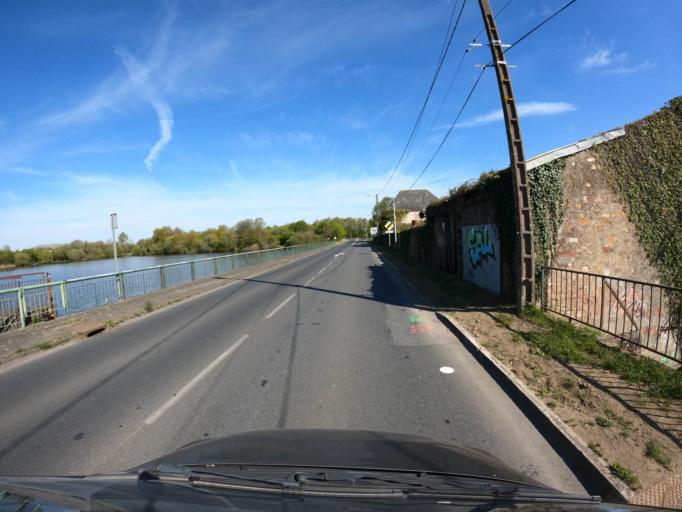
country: FR
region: Pays de la Loire
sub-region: Departement de Maine-et-Loire
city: Cholet
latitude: 47.0691
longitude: -0.9077
